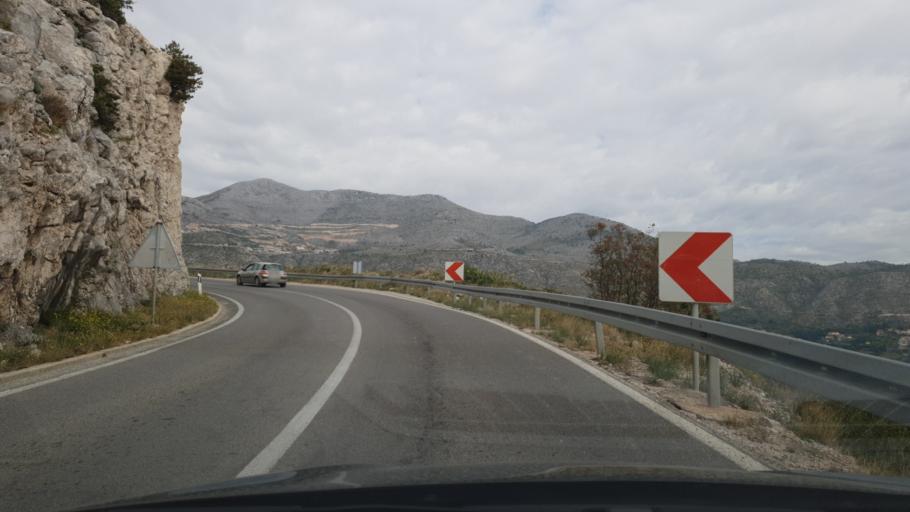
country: HR
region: Dubrovacko-Neretvanska
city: Cibaca
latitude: 42.6402
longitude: 18.1673
